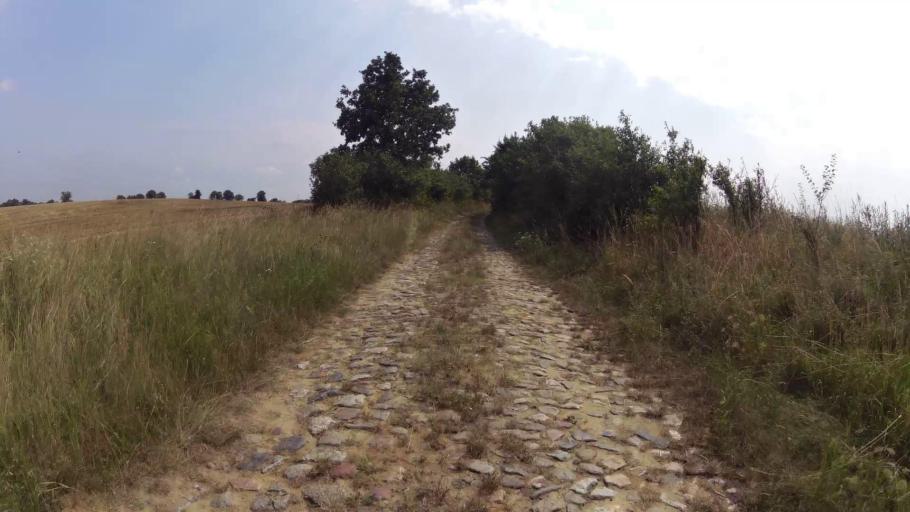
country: PL
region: West Pomeranian Voivodeship
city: Trzcinsko Zdroj
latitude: 52.8963
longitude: 14.5231
